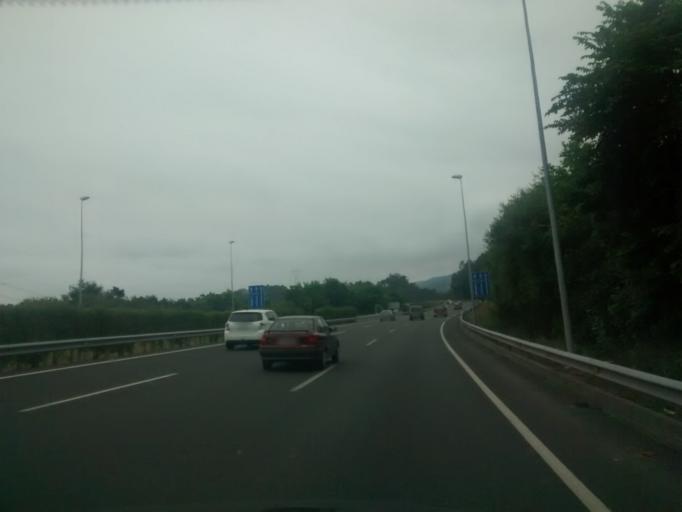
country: ES
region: Cantabria
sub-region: Provincia de Cantabria
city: Luzmela
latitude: 43.3254
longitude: -4.1877
